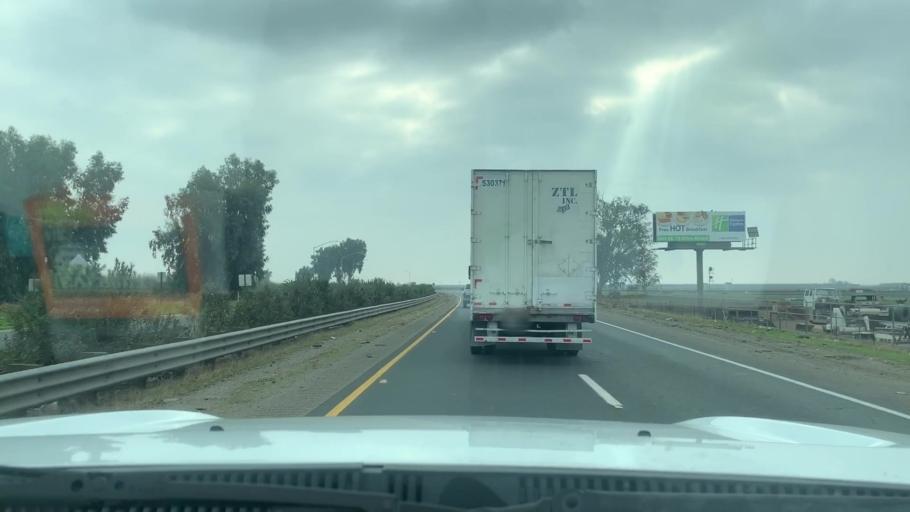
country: US
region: California
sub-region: Tulare County
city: Tipton
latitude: 36.0500
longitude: -119.3113
